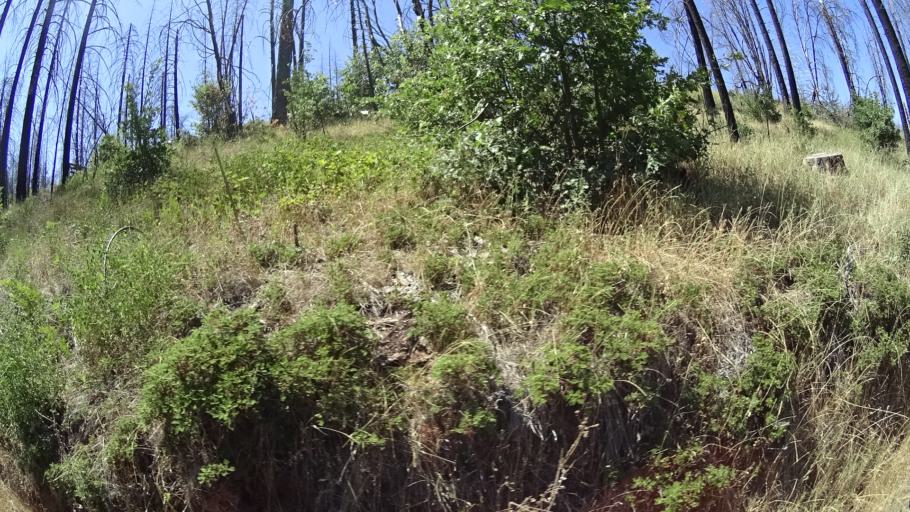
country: US
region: California
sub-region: Calaveras County
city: Mountain Ranch
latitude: 38.2870
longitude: -120.5355
